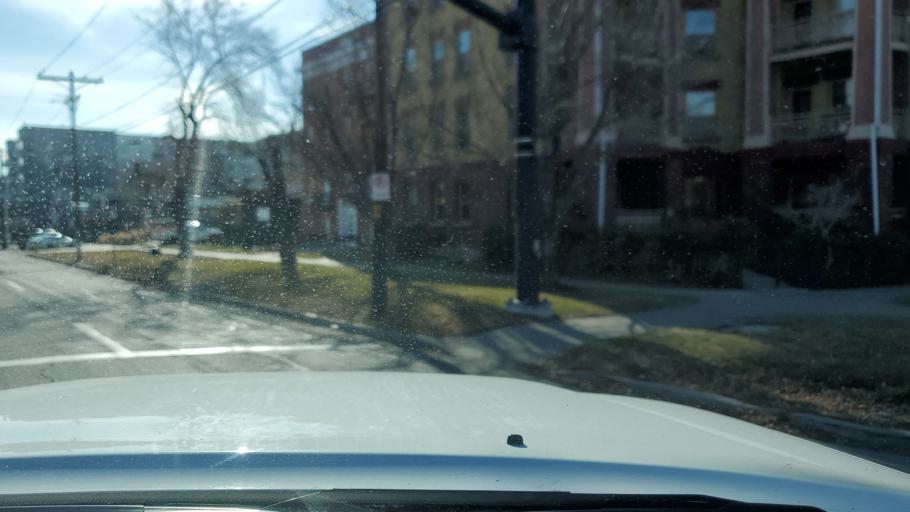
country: US
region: Utah
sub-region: Salt Lake County
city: Salt Lake City
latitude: 40.7628
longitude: -111.8769
